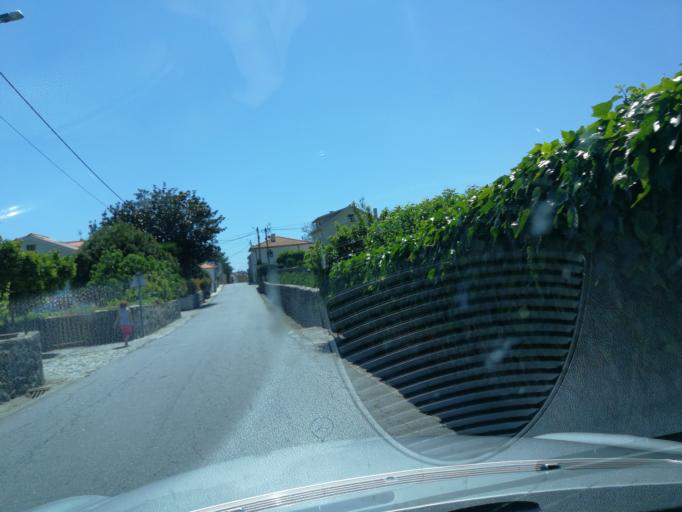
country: PT
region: Viana do Castelo
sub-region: Viana do Castelo
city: Meadela
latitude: 41.7335
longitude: -8.7862
